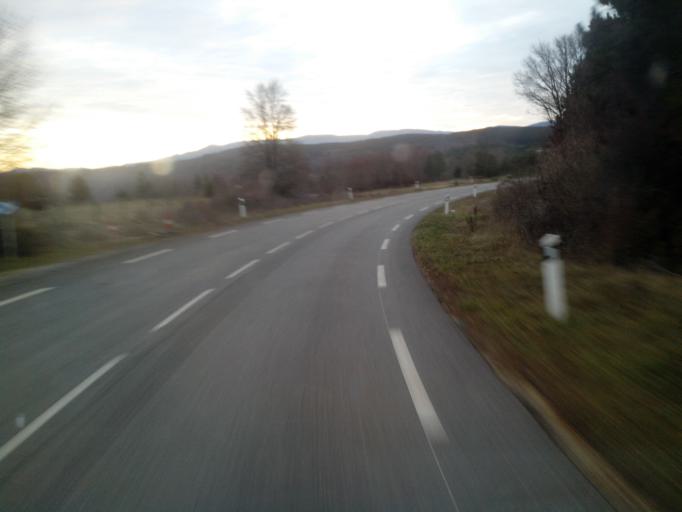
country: FR
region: Languedoc-Roussillon
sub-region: Departement de la Lozere
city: Florac
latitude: 44.2479
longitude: 3.6260
